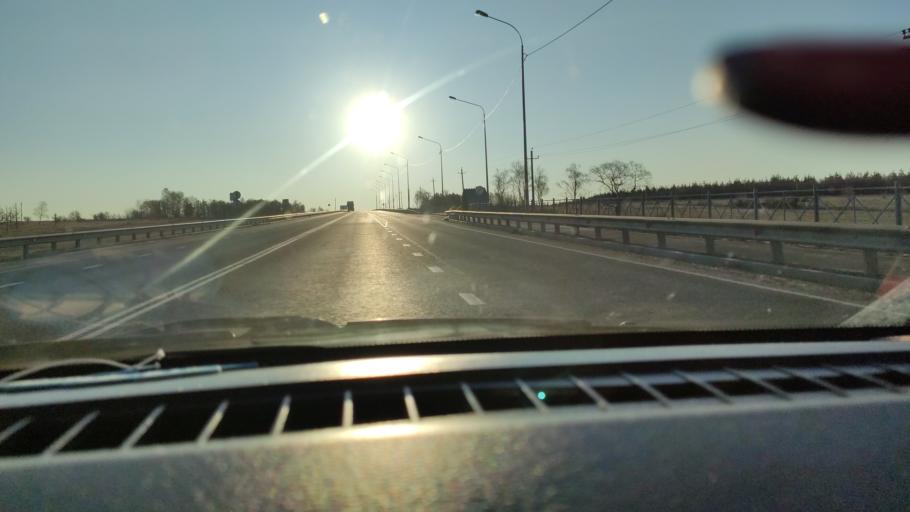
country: RU
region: Saratov
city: Shikhany
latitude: 52.1602
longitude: 47.0861
